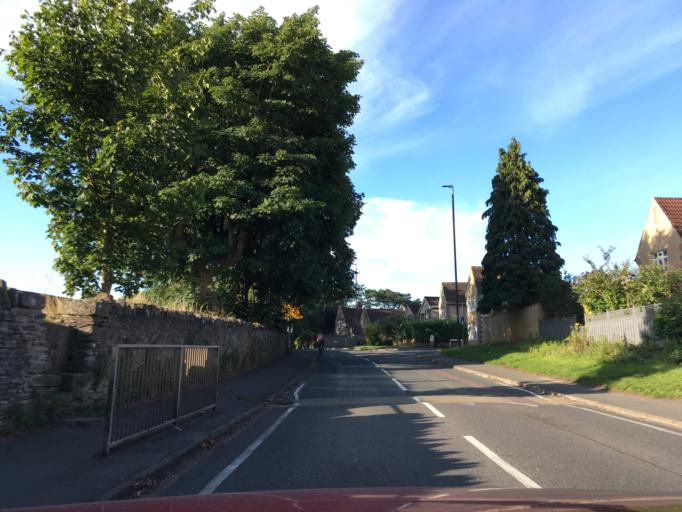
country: GB
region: England
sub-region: South Gloucestershire
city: Mangotsfield
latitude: 51.4818
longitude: -2.4846
